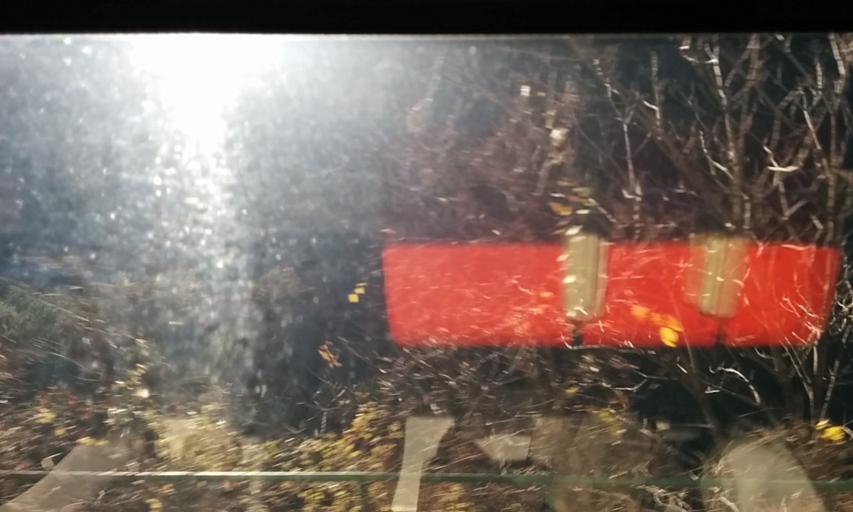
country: JP
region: Nagano
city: Ina
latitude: 35.7600
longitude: 137.7086
